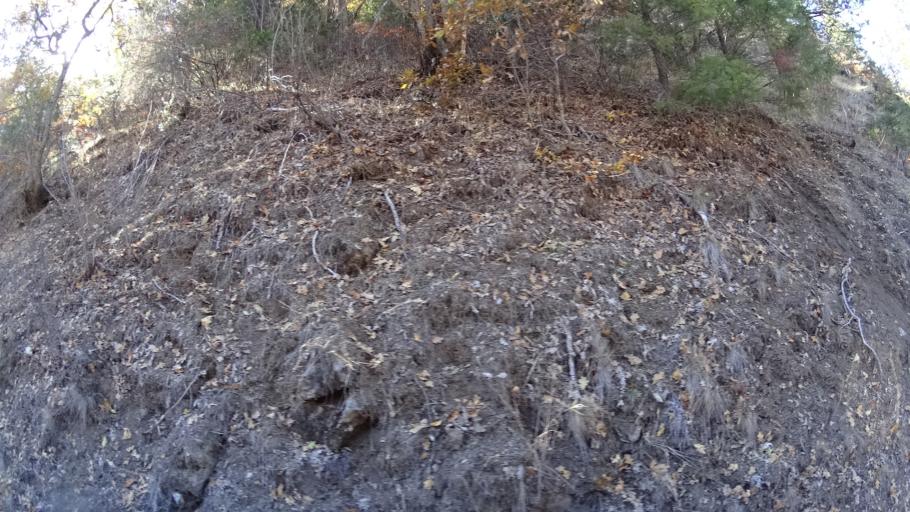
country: US
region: California
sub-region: Siskiyou County
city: Yreka
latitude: 41.8577
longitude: -122.7763
